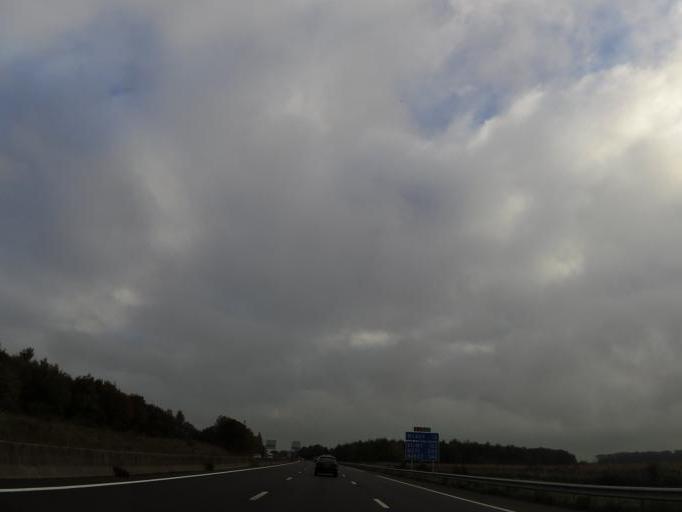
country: FR
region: Ile-de-France
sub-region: Departement de Seine-et-Marne
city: Bailly-Romainvilliers
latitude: 48.8430
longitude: 2.8258
